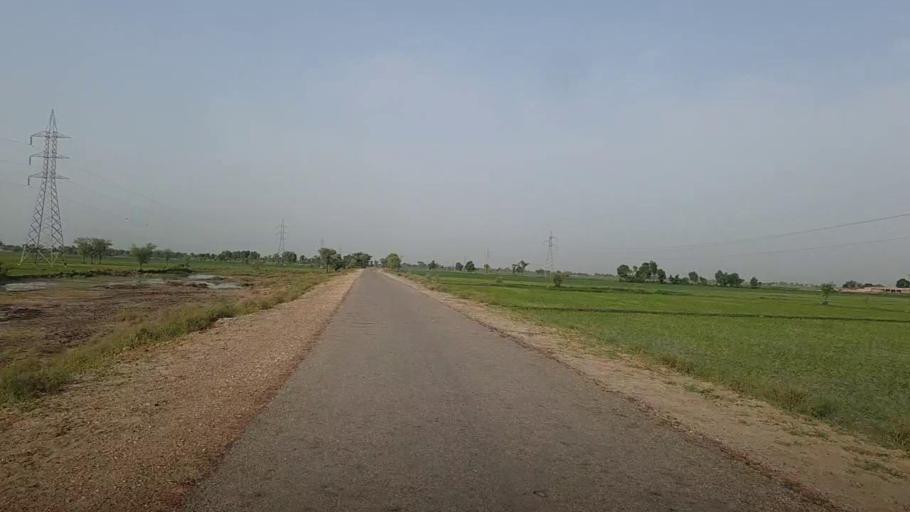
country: PK
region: Sindh
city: Mehar
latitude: 27.1406
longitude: 67.7929
